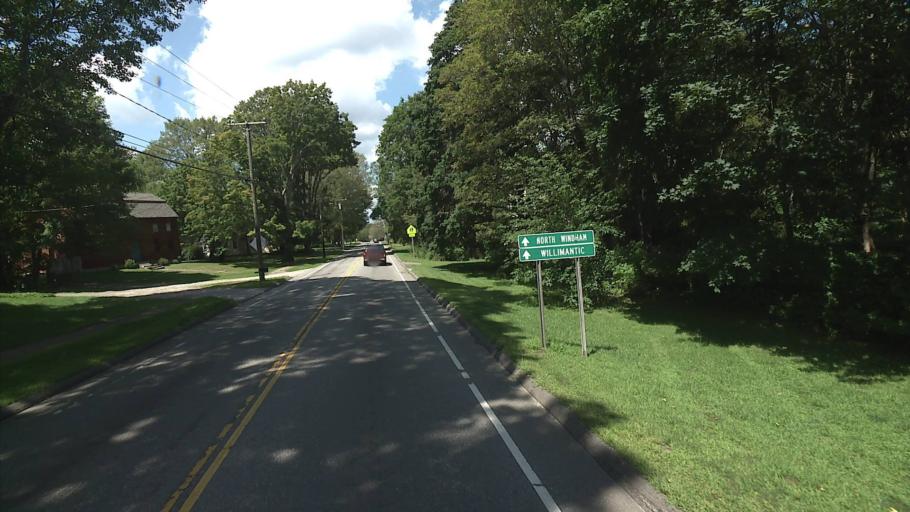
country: US
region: Connecticut
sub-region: Windham County
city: Windham
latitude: 41.7003
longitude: -72.1584
